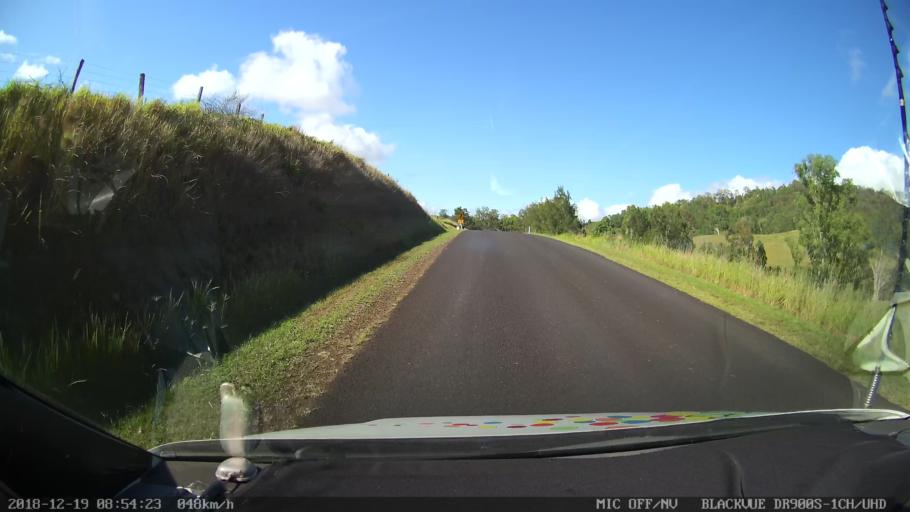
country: AU
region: New South Wales
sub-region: Kyogle
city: Kyogle
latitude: -28.4097
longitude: 152.9788
